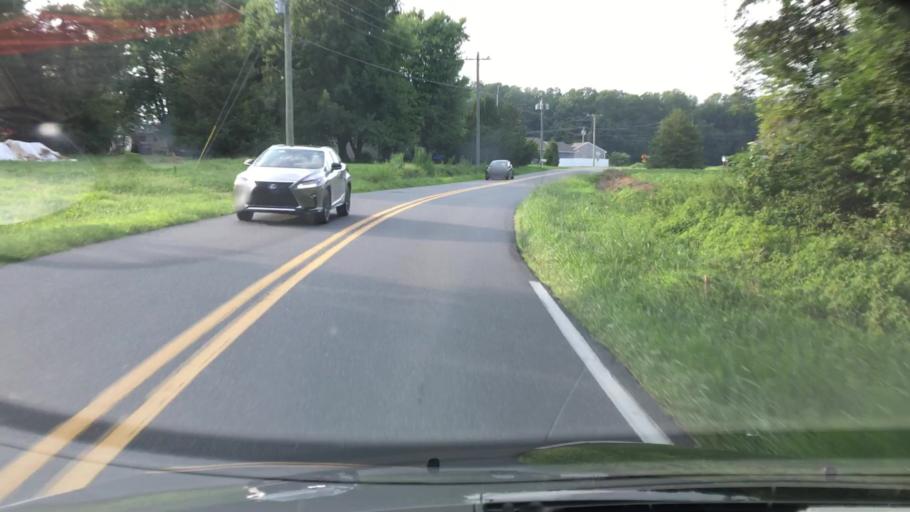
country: US
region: Maryland
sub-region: Worcester County
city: Ocean Pines
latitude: 38.4759
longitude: -75.1400
